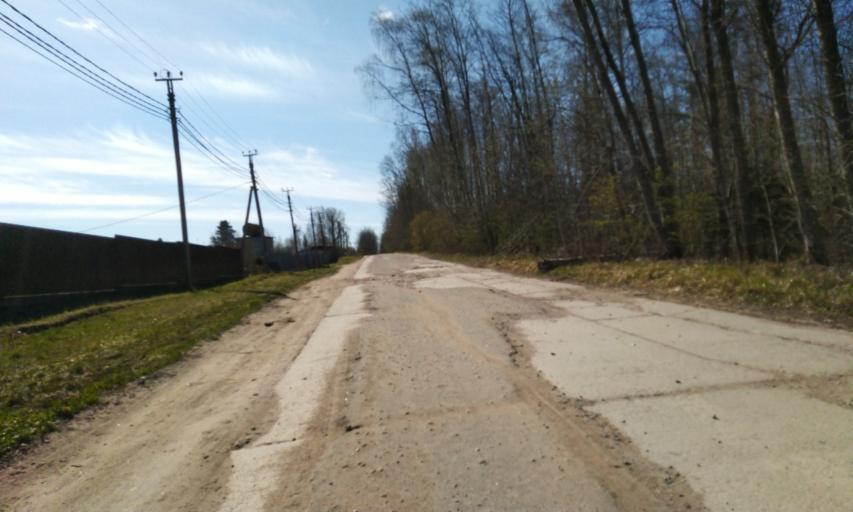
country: RU
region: Leningrad
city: Garbolovo
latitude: 60.3911
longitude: 30.4795
